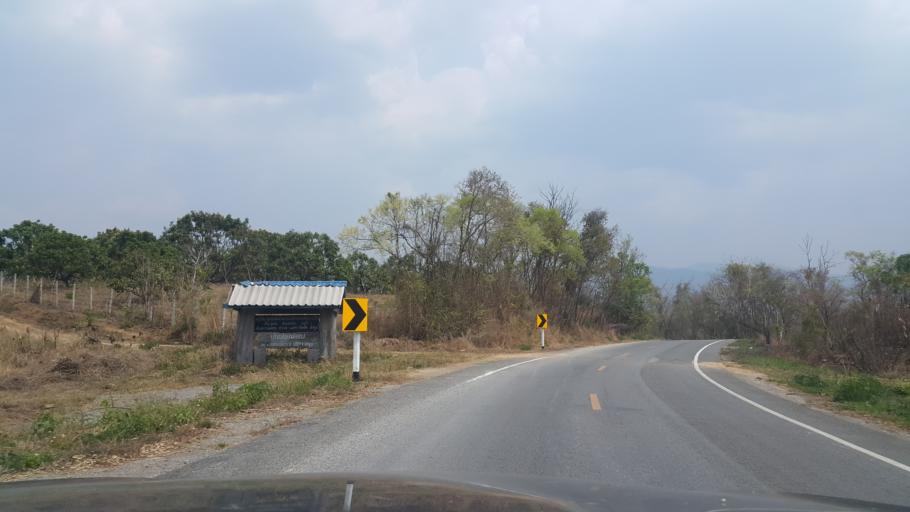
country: TH
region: Lamphun
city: Ban Hong
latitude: 18.2648
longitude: 98.9213
